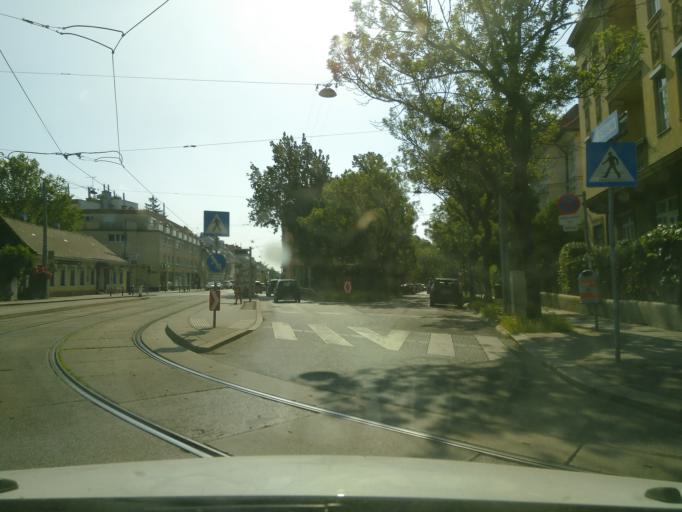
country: AT
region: Lower Austria
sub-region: Politischer Bezirk Modling
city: Perchtoldsdorf
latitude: 48.1873
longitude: 16.2819
